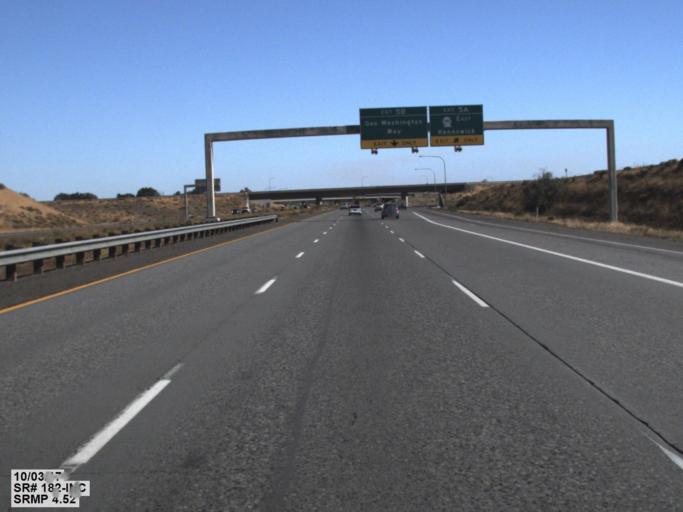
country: US
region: Washington
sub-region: Benton County
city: Richland
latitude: 46.2587
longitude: -119.2720
